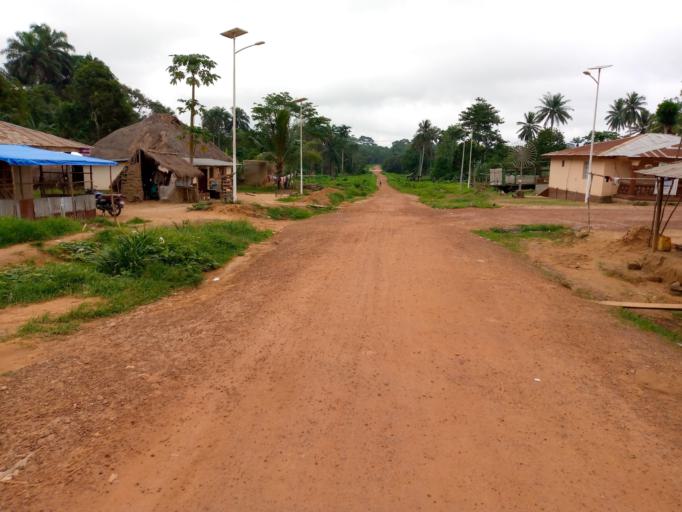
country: SL
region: Southern Province
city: Sumbuya
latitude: 7.5629
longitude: -12.0882
